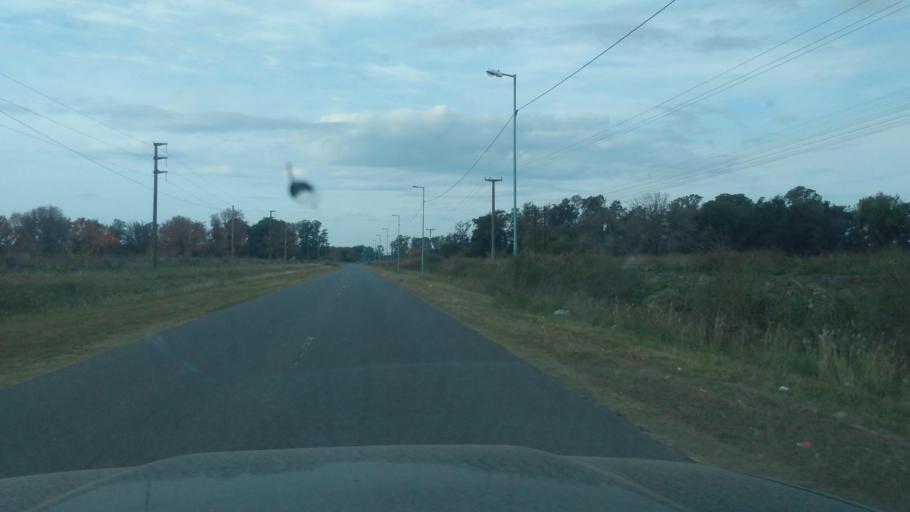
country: AR
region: Buenos Aires
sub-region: Partido de Lujan
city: Lujan
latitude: -34.5982
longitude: -59.1669
